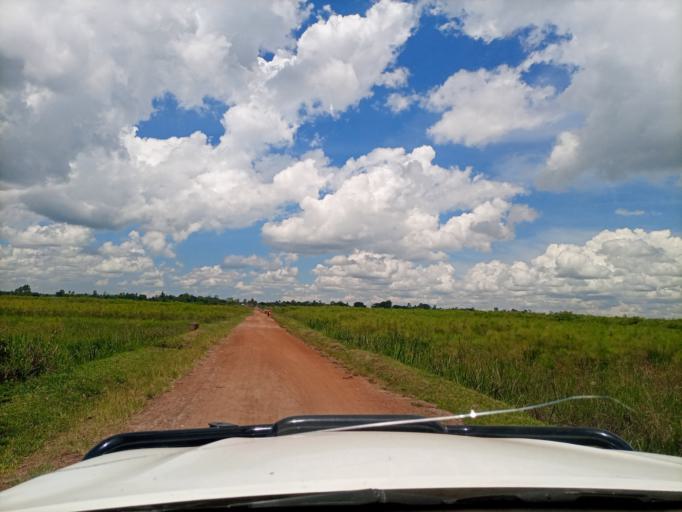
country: UG
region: Eastern Region
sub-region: Tororo District
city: Tororo
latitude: 0.6392
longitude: 33.9936
